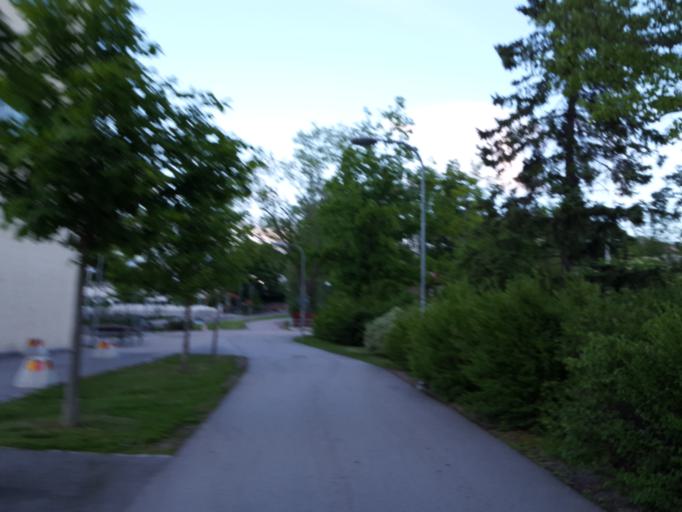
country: SE
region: Uppsala
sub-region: Uppsala Kommun
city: Uppsala
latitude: 59.8503
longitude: 17.6312
